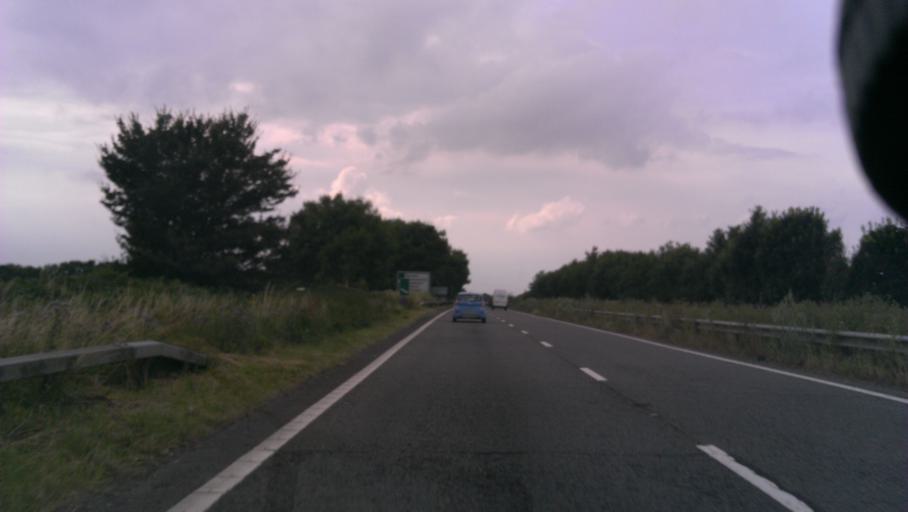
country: GB
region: England
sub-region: Kent
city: Wootton
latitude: 51.1934
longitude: 1.1858
